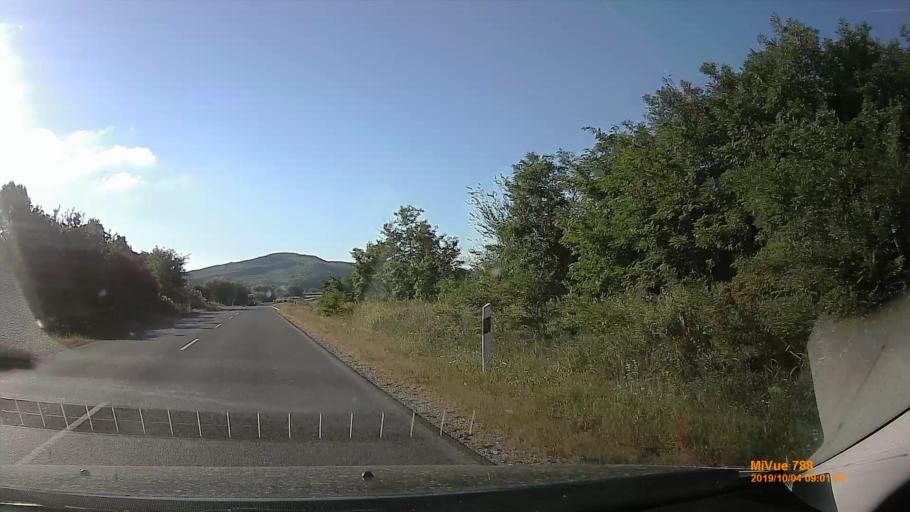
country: HU
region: Somogy
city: Karad
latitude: 46.7381
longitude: 17.7749
